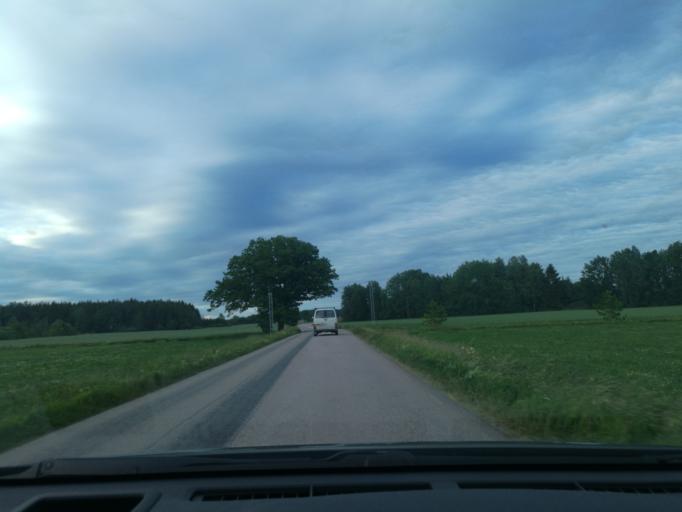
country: SE
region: Vaestmanland
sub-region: Hallstahammars Kommun
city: Kolback
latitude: 59.5488
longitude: 16.3287
